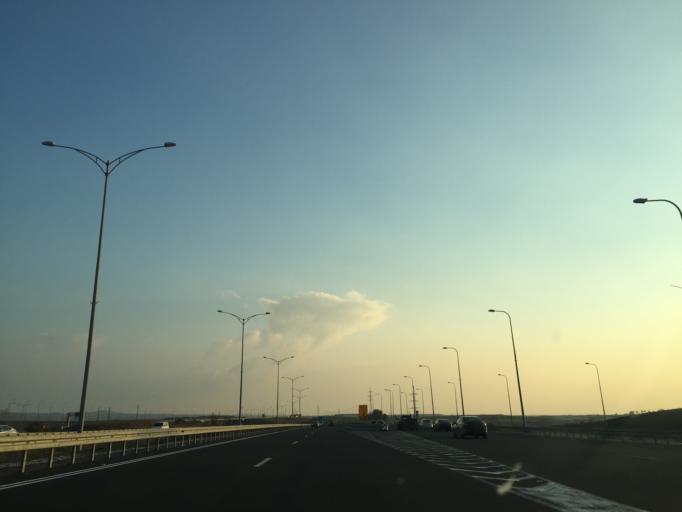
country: IL
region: Southern District
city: Lehavim
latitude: 31.4018
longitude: 34.7886
